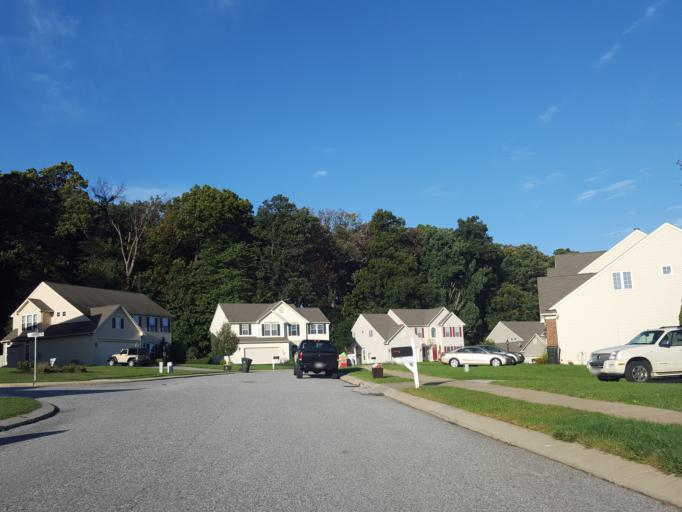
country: US
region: Pennsylvania
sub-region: York County
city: Windsor
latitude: 39.9479
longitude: -76.6091
